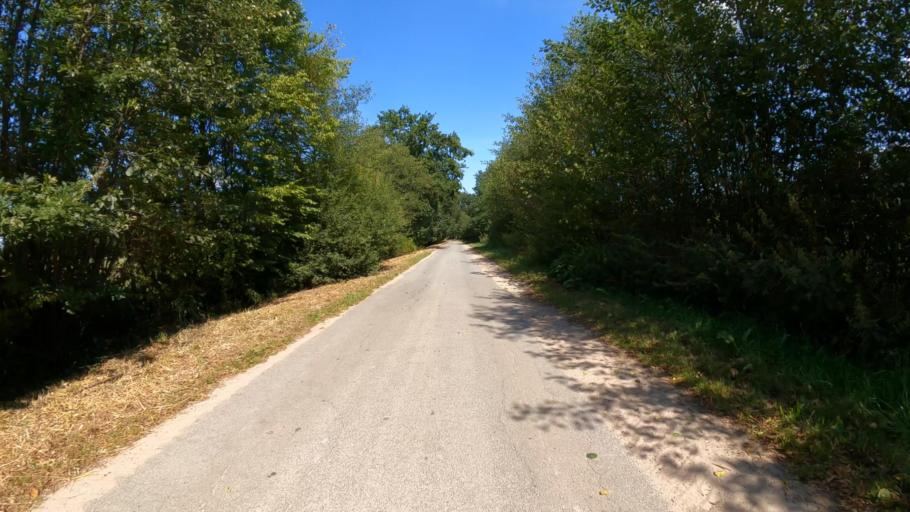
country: DE
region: Schleswig-Holstein
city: Borstel-Hohenraden
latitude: 53.7108
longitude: 9.8289
